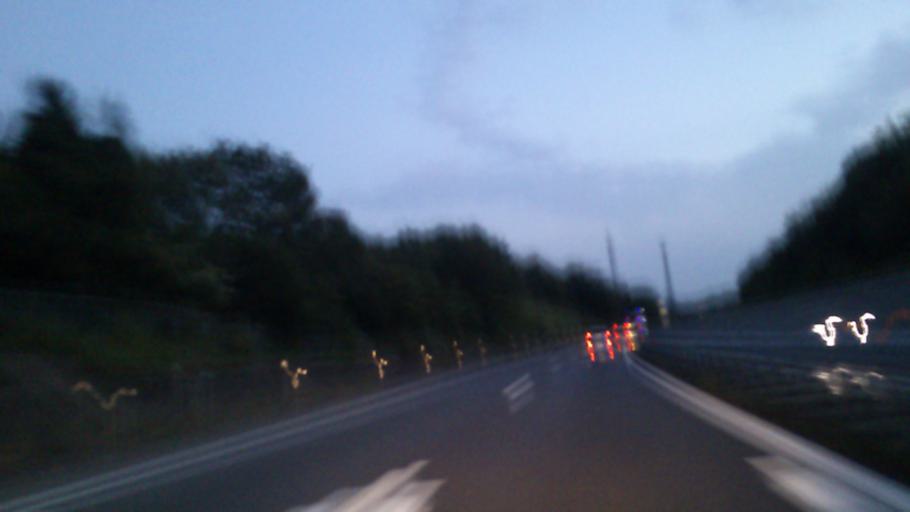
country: JP
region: Aichi
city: Kasugai
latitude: 35.3138
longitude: 137.0188
